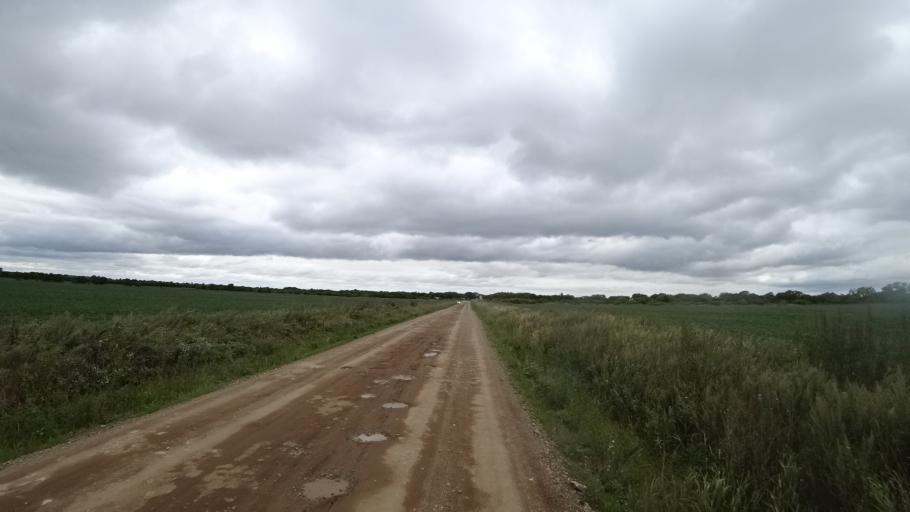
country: RU
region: Primorskiy
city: Chernigovka
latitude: 44.3439
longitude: 132.6107
